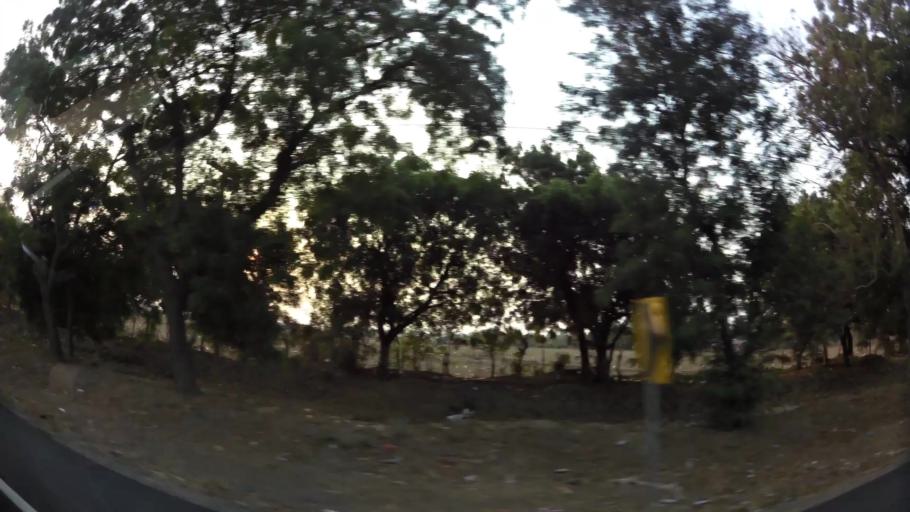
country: NI
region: Leon
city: La Paz Centro
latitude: 12.3332
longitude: -86.6813
